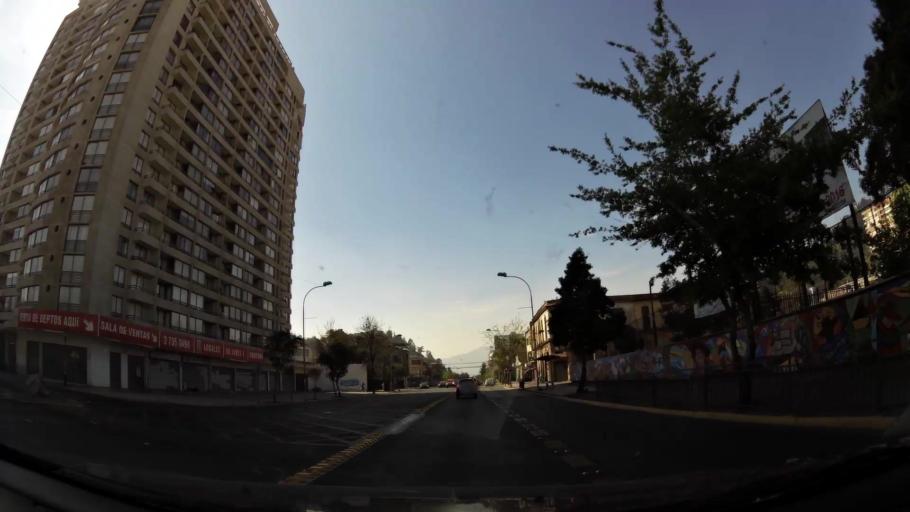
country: CL
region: Santiago Metropolitan
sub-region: Provincia de Santiago
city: Santiago
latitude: -33.4263
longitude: -70.6464
